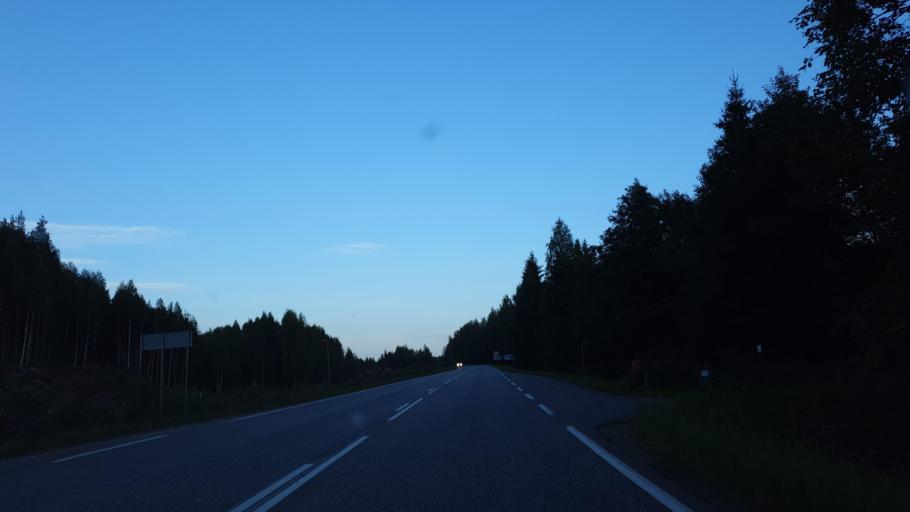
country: FI
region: Northern Savo
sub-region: Koillis-Savo
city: Kaavi
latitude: 62.9252
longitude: 28.6841
